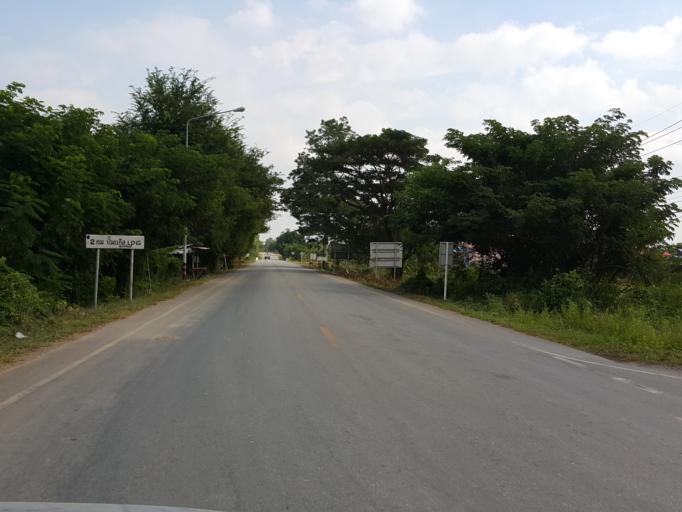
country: TH
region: Sukhothai
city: Thung Saliam
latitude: 17.3370
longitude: 99.5829
